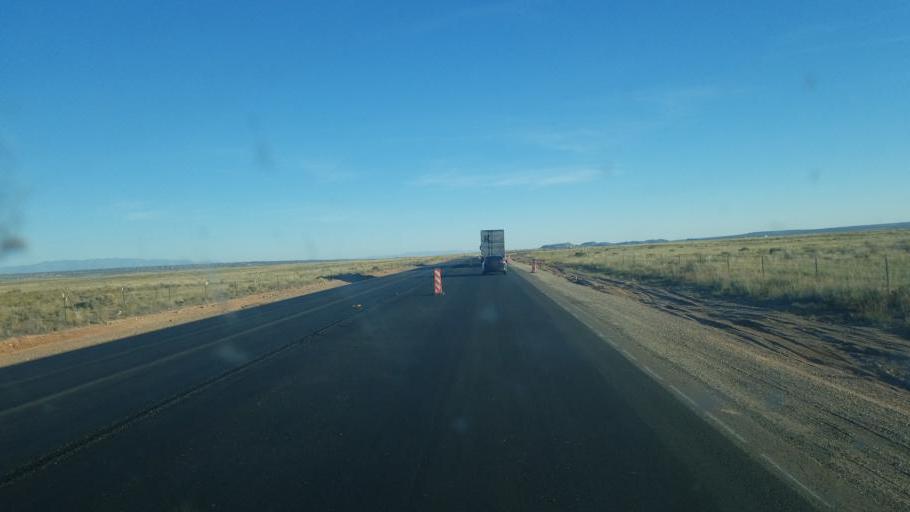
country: US
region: New Mexico
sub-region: Valencia County
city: Los Lunas
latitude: 34.8788
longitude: -107.0584
